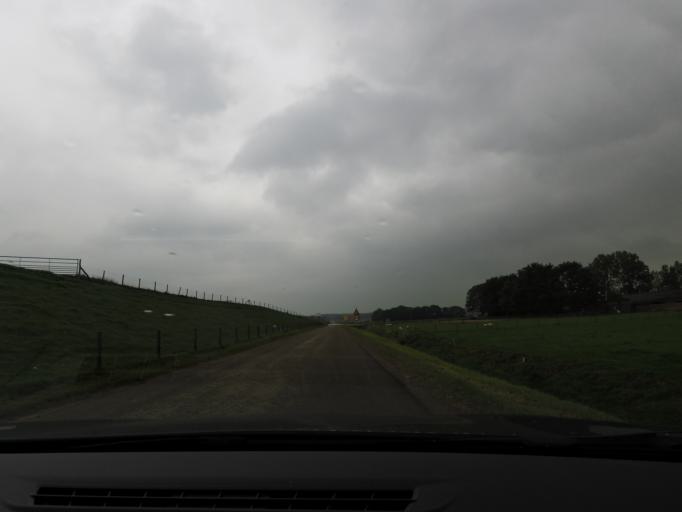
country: NL
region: South Holland
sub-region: Gemeente Spijkenisse
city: Spijkenisse
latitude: 51.8130
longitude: 4.3190
